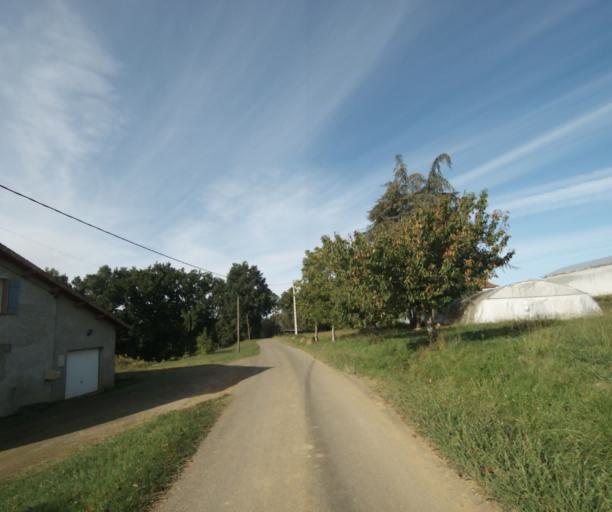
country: FR
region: Midi-Pyrenees
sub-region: Departement du Gers
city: Eauze
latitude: 43.9017
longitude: 0.1328
